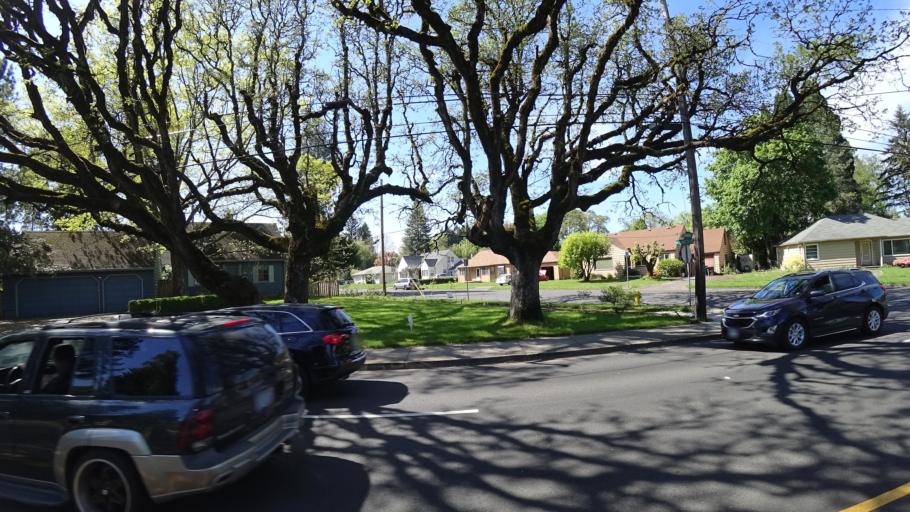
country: US
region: Oregon
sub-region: Washington County
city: Hillsboro
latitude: 45.5236
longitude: -122.9727
